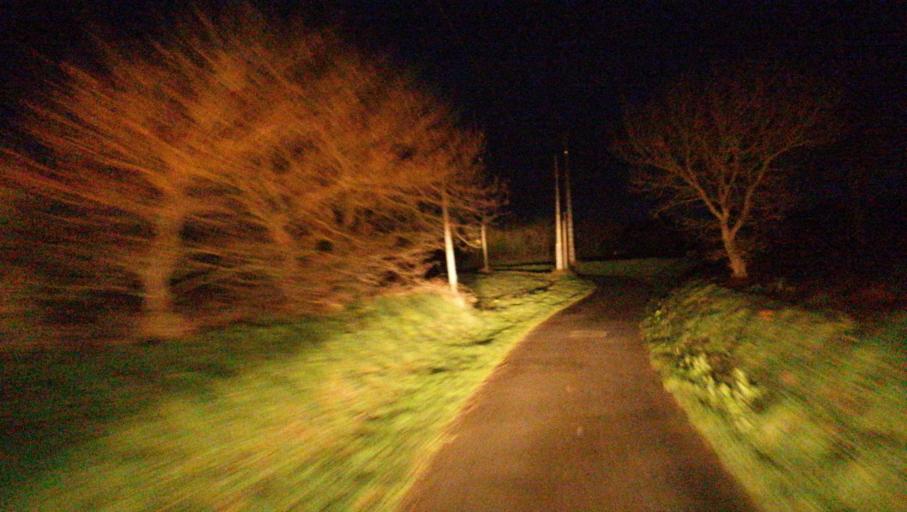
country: FR
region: Brittany
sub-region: Departement des Cotes-d'Armor
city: Plehedel
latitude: 48.6826
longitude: -3.0355
